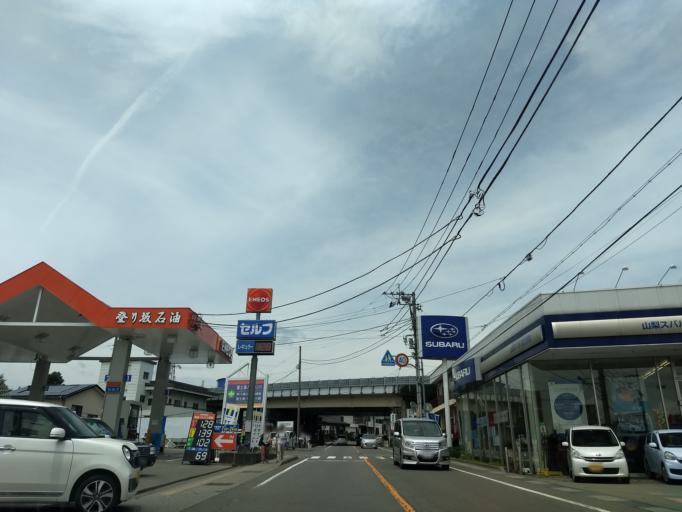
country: JP
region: Yamanashi
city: Fujikawaguchiko
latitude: 35.4901
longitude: 138.7818
